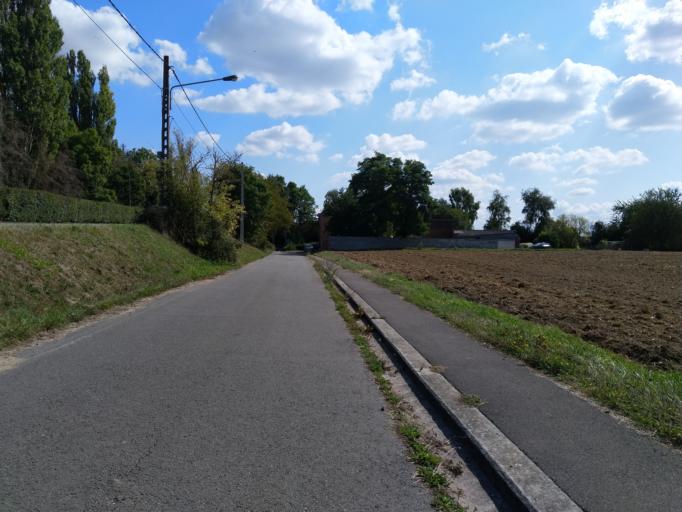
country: BE
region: Wallonia
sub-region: Province du Hainaut
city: Chasse Royale
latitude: 50.4297
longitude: 3.9330
